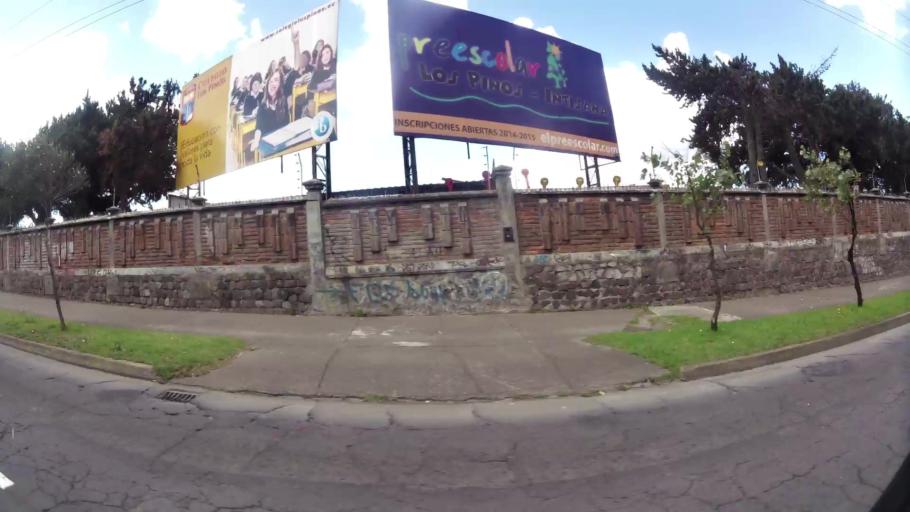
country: EC
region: Pichincha
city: Quito
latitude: -0.1531
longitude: -78.4977
